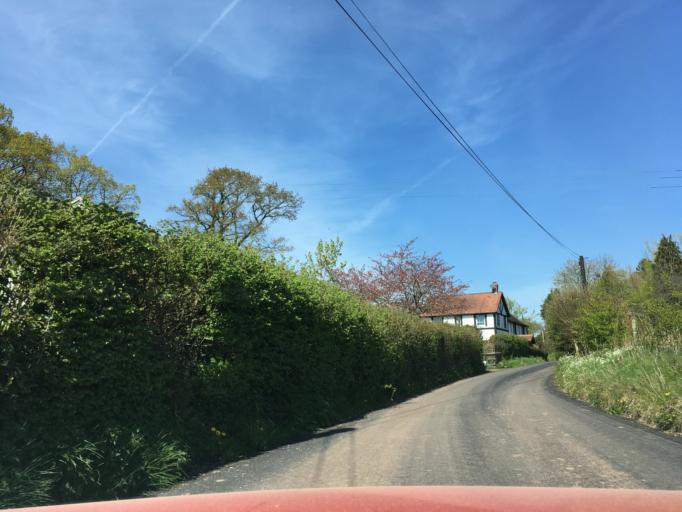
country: GB
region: Wales
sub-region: Monmouthshire
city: Llanarth
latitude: 51.7715
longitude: -2.8312
